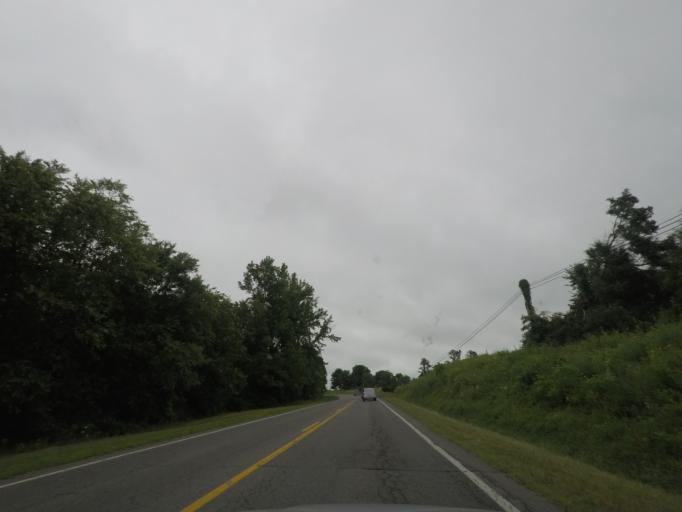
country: US
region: Virginia
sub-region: Fluvanna County
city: Palmyra
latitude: 37.8043
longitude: -78.2388
